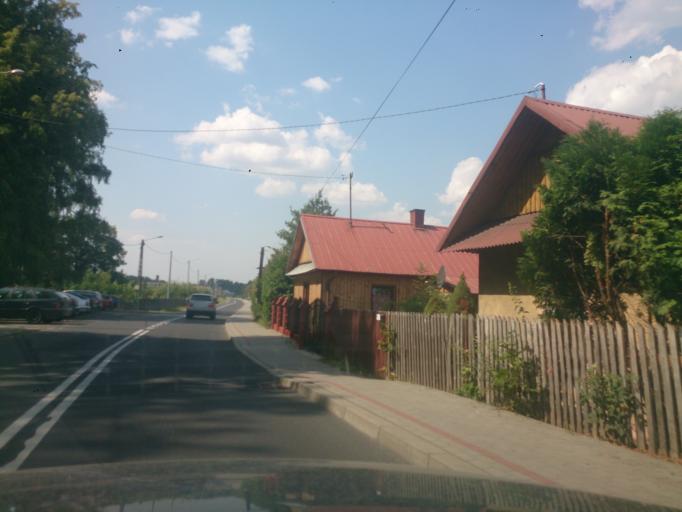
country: PL
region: Subcarpathian Voivodeship
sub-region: Powiat kolbuszowski
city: Majdan Krolewski
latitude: 50.3797
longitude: 21.7431
